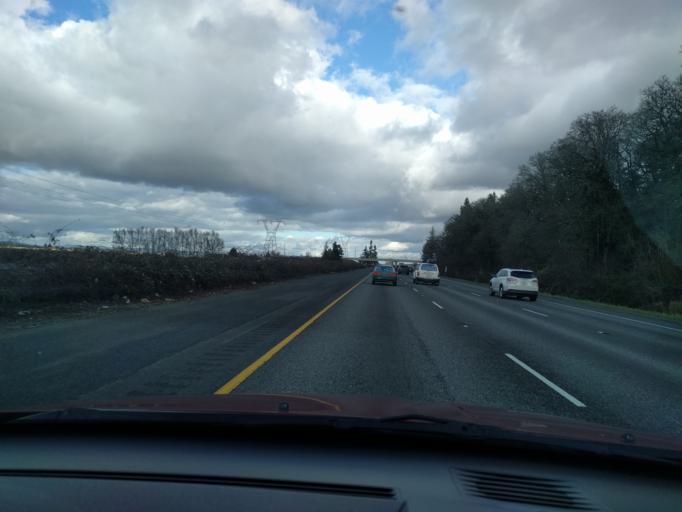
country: US
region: Oregon
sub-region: Marion County
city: Gervais
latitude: 45.0692
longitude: -122.9622
